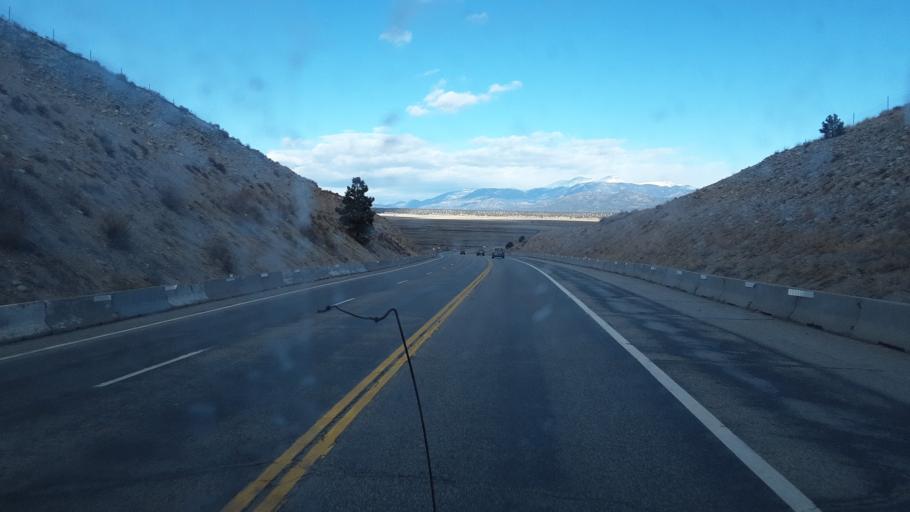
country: US
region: Colorado
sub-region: Chaffee County
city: Buena Vista
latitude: 38.7052
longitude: -106.0905
